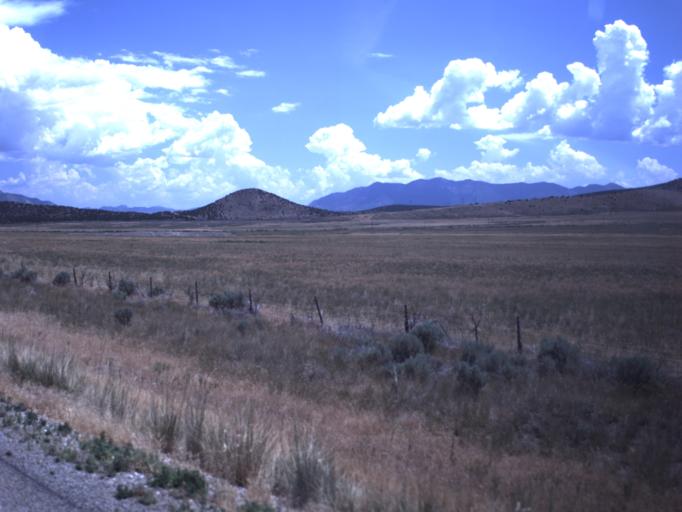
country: US
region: Utah
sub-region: Juab County
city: Nephi
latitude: 39.6801
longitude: -112.0157
